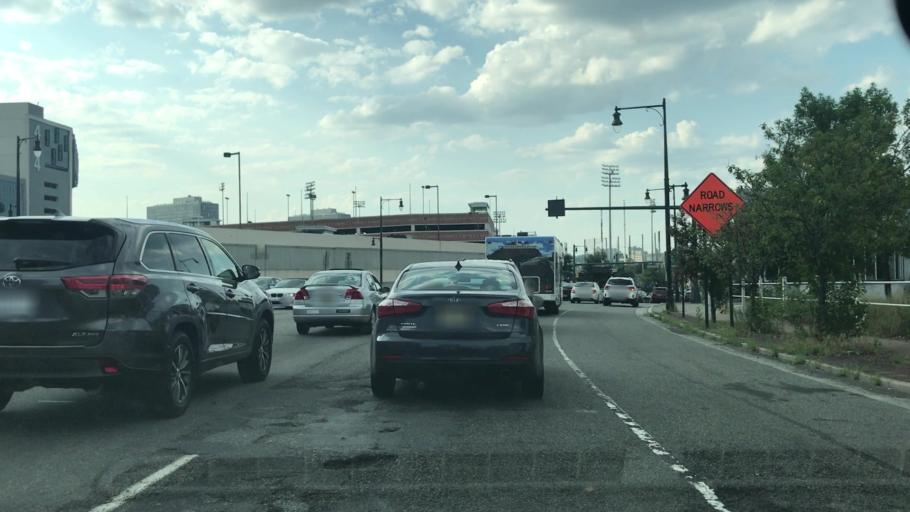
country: US
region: New Jersey
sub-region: Hudson County
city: East Newark
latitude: 40.7435
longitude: -74.1671
